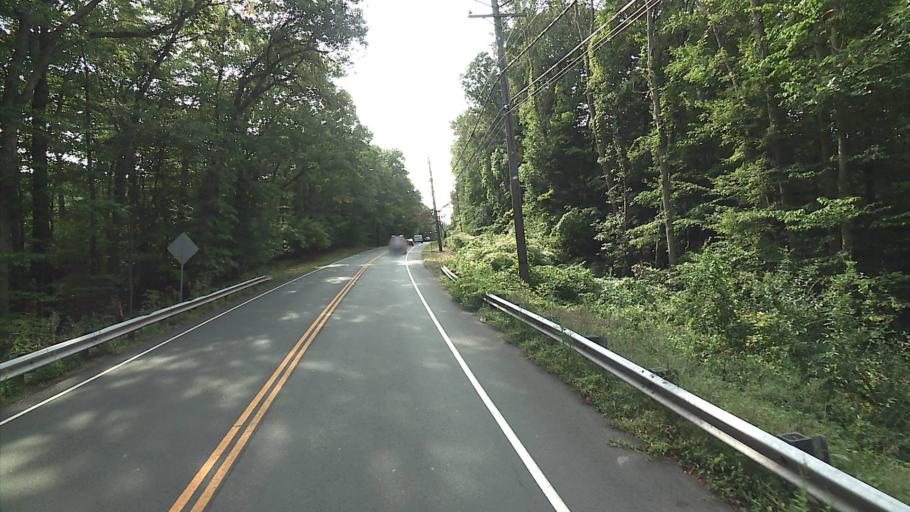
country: US
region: Connecticut
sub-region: Fairfield County
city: New Canaan
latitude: 41.1476
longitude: -73.4813
